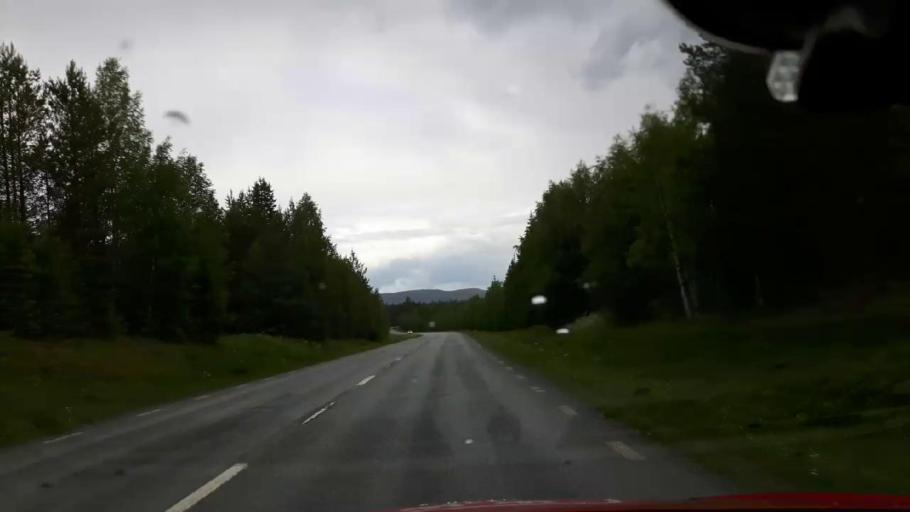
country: SE
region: Jaemtland
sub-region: Krokoms Kommun
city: Krokom
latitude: 63.4247
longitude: 14.2169
